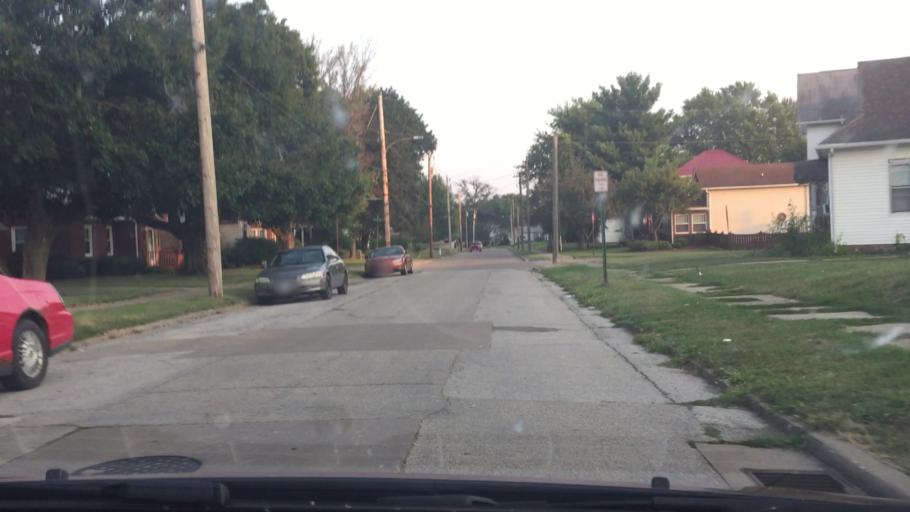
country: US
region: Iowa
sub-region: Muscatine County
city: Muscatine
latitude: 41.4352
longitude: -91.0484
